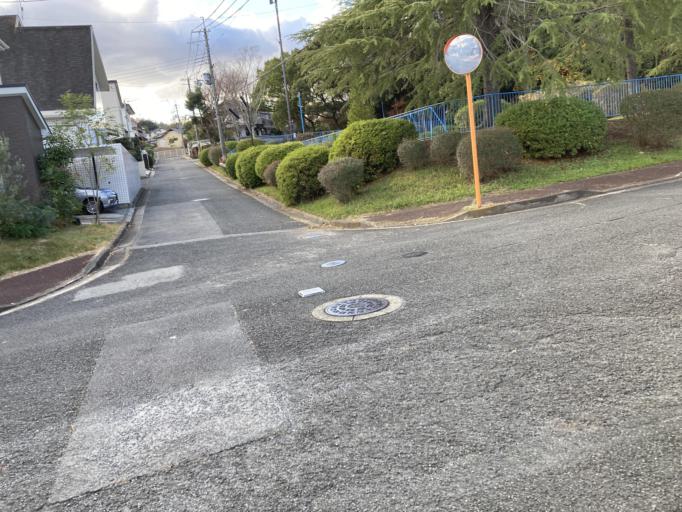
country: JP
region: Nara
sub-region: Ikoma-shi
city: Ikoma
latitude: 34.6860
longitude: 135.7273
